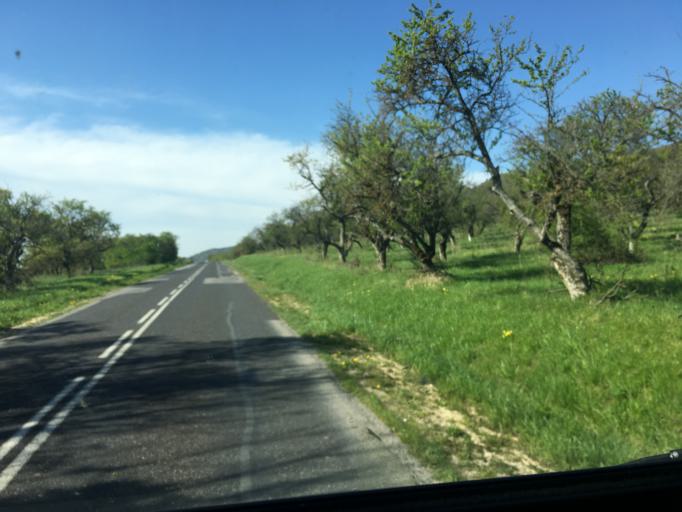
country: FR
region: Lorraine
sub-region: Departement de la Meuse
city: Vigneulles-les-Hattonchatel
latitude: 48.9234
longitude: 5.6849
